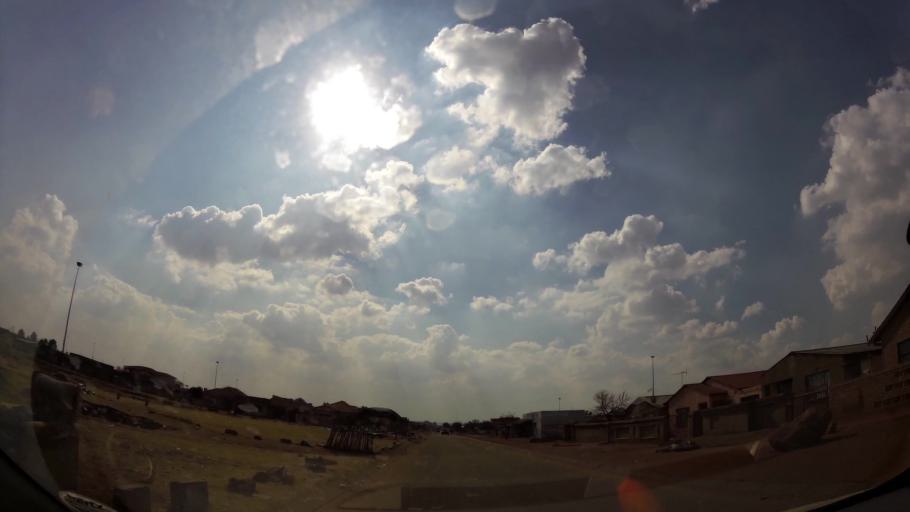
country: ZA
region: Gauteng
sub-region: Ekurhuleni Metropolitan Municipality
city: Germiston
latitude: -26.3520
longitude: 28.1654
